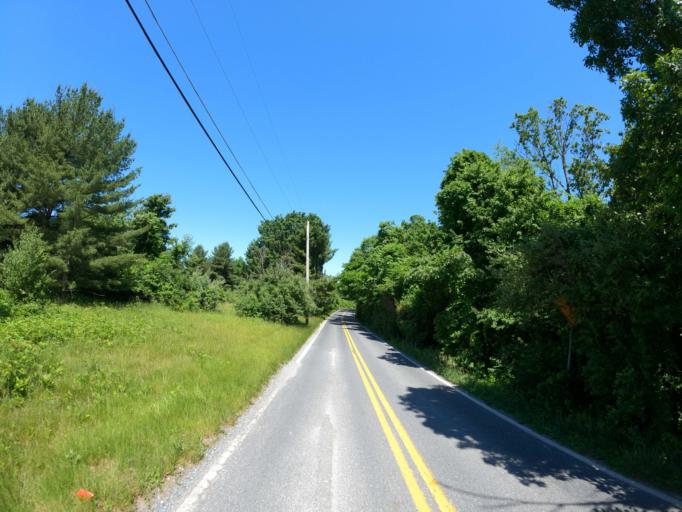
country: US
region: Maryland
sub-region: Montgomery County
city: Clarksburg
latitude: 39.2581
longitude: -77.2771
